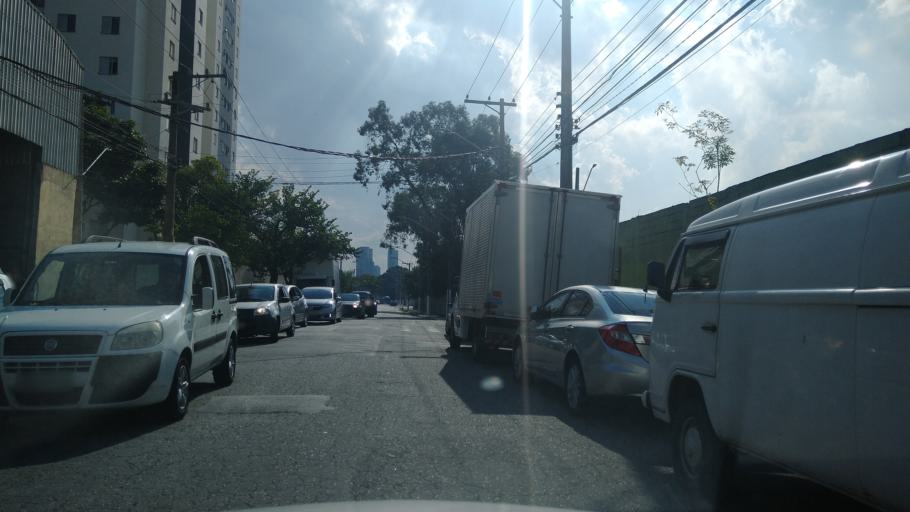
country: BR
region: Sao Paulo
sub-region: Guarulhos
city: Guarulhos
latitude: -23.5128
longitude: -46.5684
